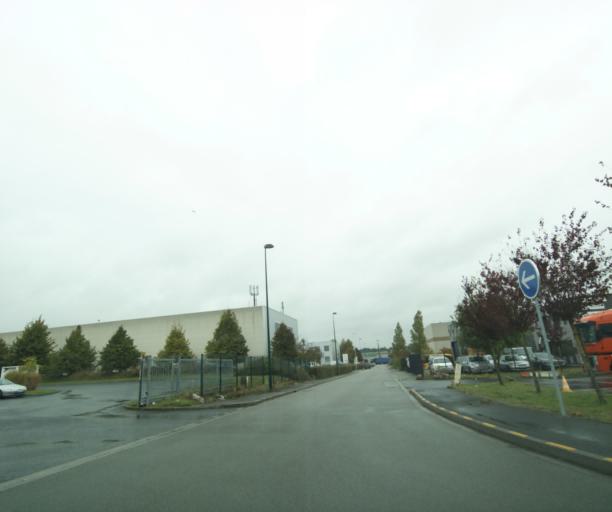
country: FR
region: Nord-Pas-de-Calais
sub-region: Departement du Nord
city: Roncq
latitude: 50.7536
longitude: 3.1307
